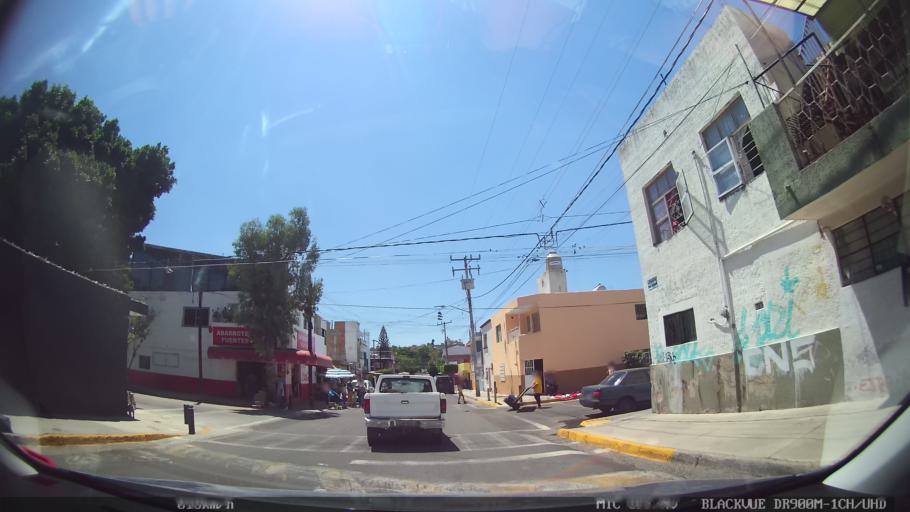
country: MX
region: Jalisco
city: Tlaquepaque
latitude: 20.6897
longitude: -103.2861
